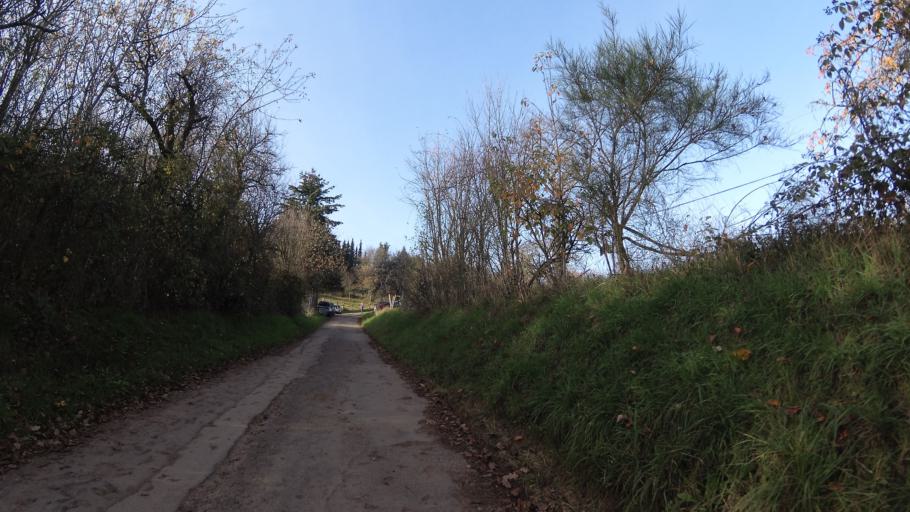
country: DE
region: Saarland
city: Hangard
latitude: 49.3843
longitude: 7.2009
